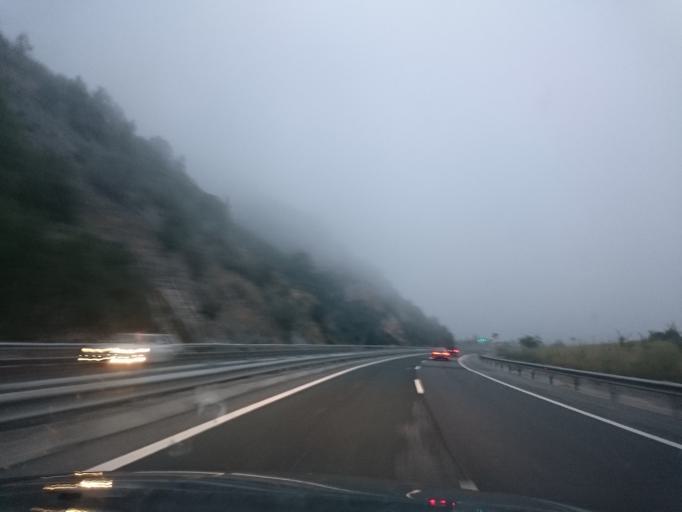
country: ES
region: Castille and Leon
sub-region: Provincia de Leon
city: Sena de Luna
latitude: 42.9851
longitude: -5.8253
